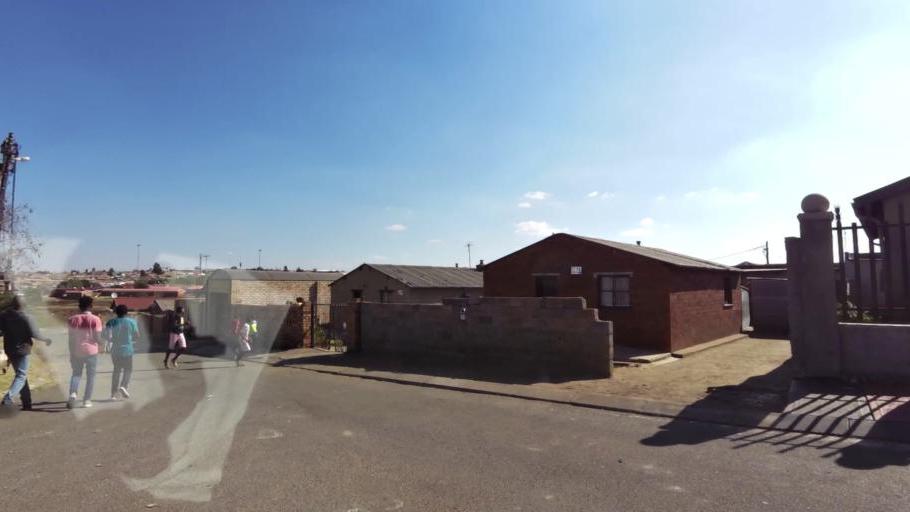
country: ZA
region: Gauteng
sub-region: City of Johannesburg Metropolitan Municipality
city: Soweto
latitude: -26.2272
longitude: 27.8864
